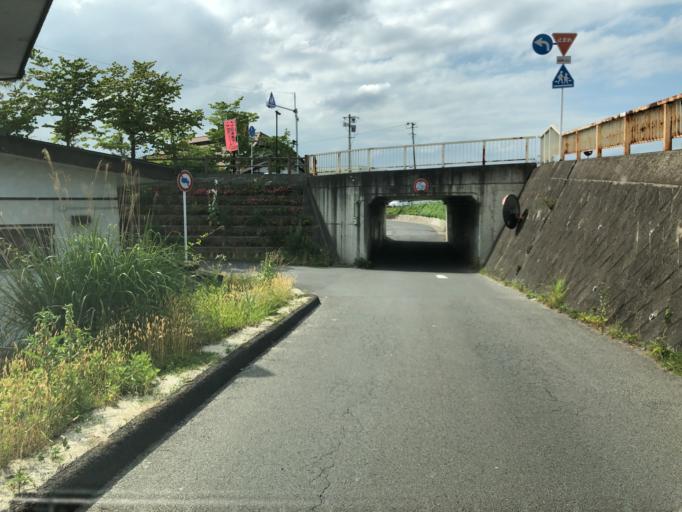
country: JP
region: Fukushima
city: Fukushima-shi
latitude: 37.7508
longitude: 140.4510
